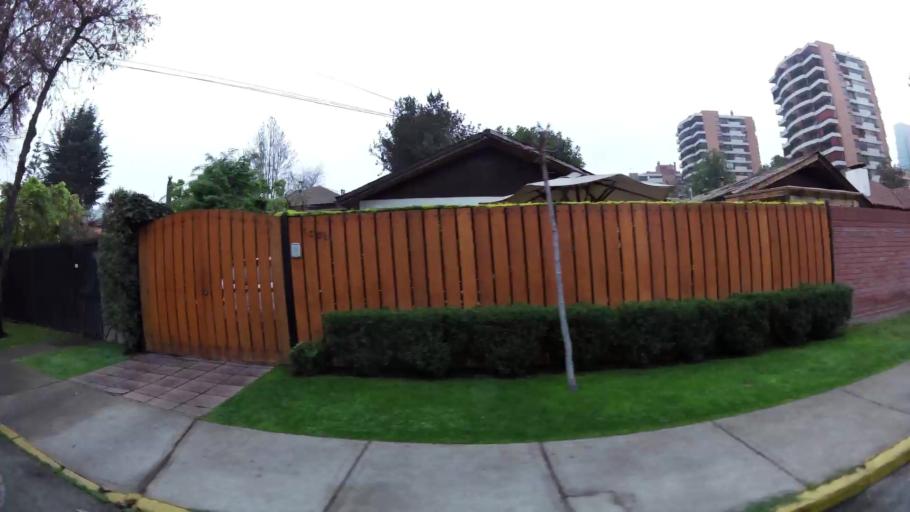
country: CL
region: Santiago Metropolitan
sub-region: Provincia de Santiago
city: Villa Presidente Frei, Nunoa, Santiago, Chile
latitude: -33.3974
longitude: -70.5790
